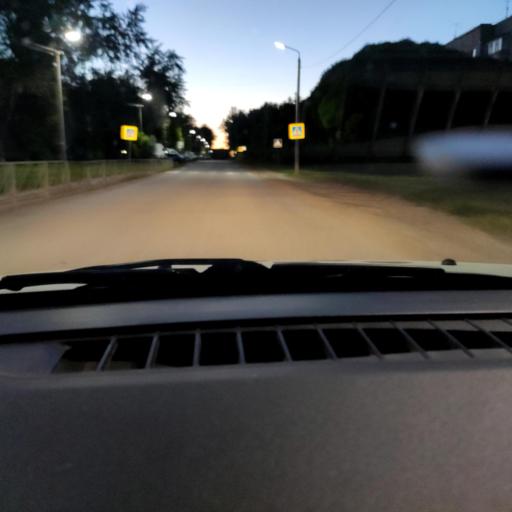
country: RU
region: Perm
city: Zvezdnyy
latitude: 57.7346
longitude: 56.3221
